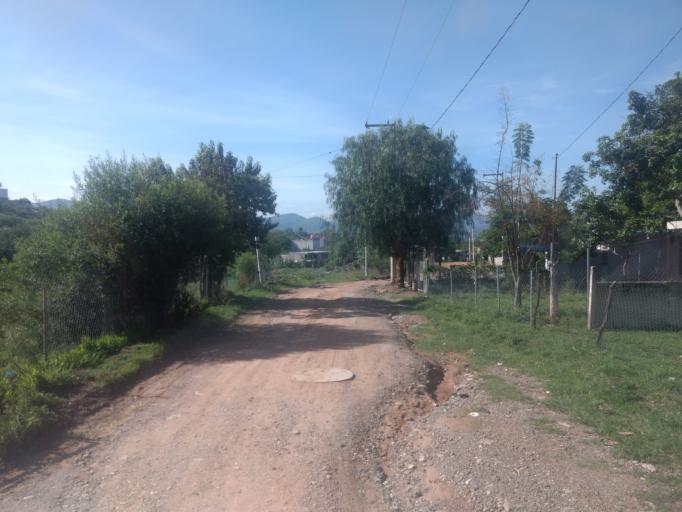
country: MX
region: Oaxaca
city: Ciudad de Huajuapam de Leon
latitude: 17.8233
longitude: -97.7861
